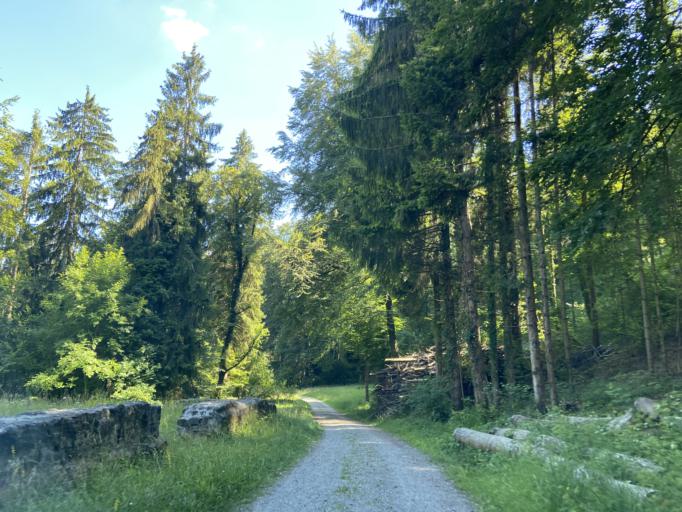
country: CH
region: Zurich
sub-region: Bezirk Winterthur
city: Wuelflingen (Kreis 6) / Niederfeld
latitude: 47.5066
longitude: 8.6655
